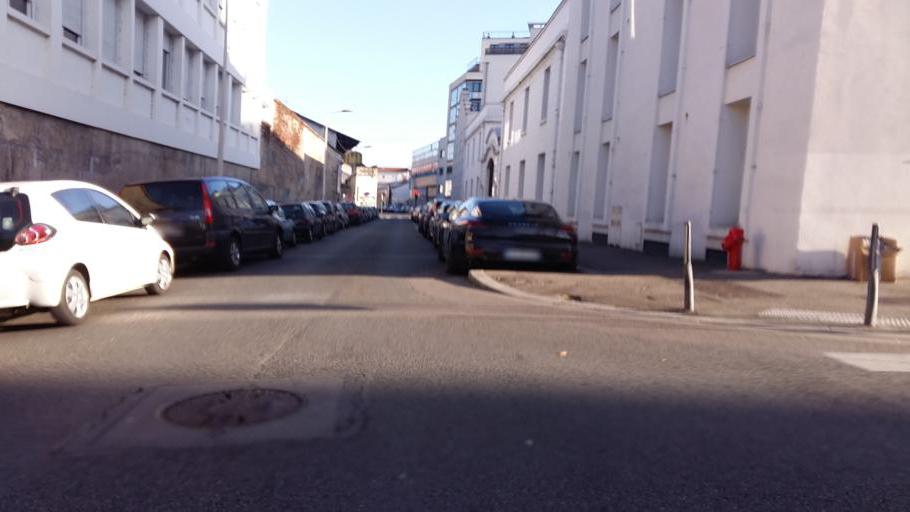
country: FR
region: Rhone-Alpes
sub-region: Departement du Rhone
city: Lyon
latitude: 45.7446
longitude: 4.8339
